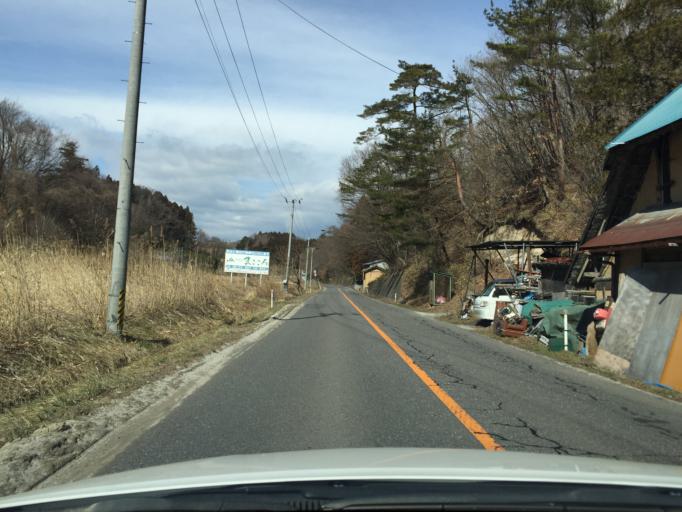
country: JP
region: Fukushima
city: Funehikimachi-funehiki
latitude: 37.4065
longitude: 140.5475
